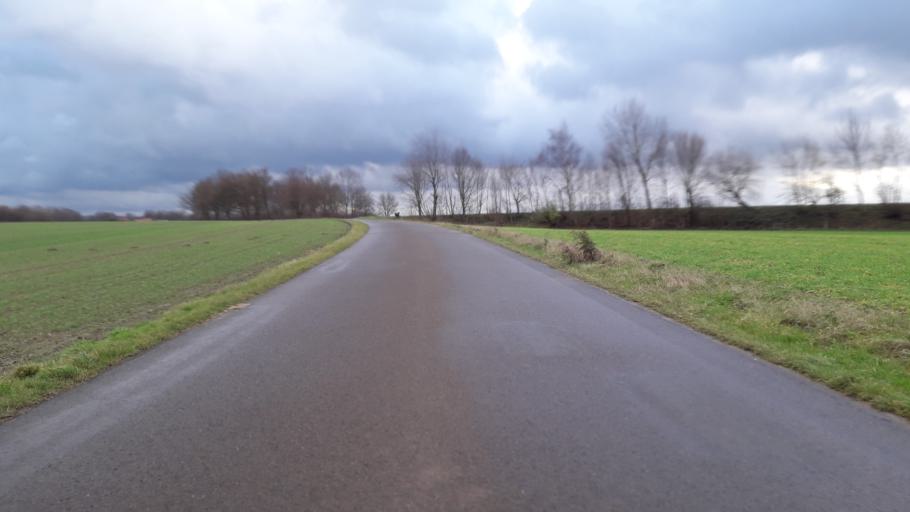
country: DE
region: North Rhine-Westphalia
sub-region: Regierungsbezirk Detmold
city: Petershagen
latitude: 52.3328
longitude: 8.9594
